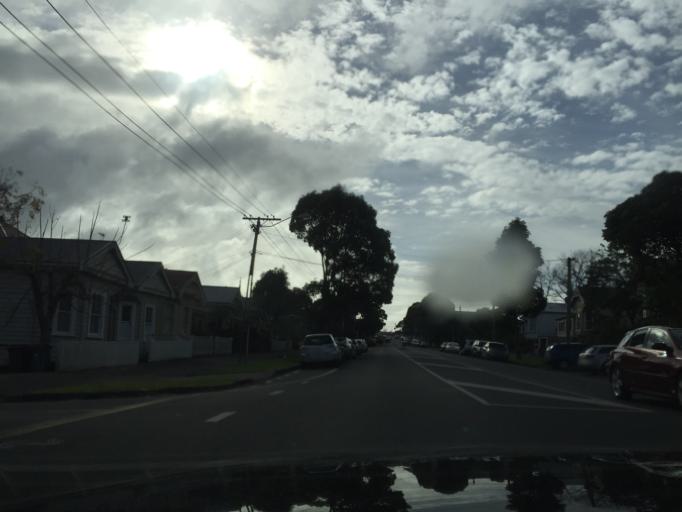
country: NZ
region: Auckland
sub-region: Auckland
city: Auckland
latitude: -36.8607
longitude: 174.7445
